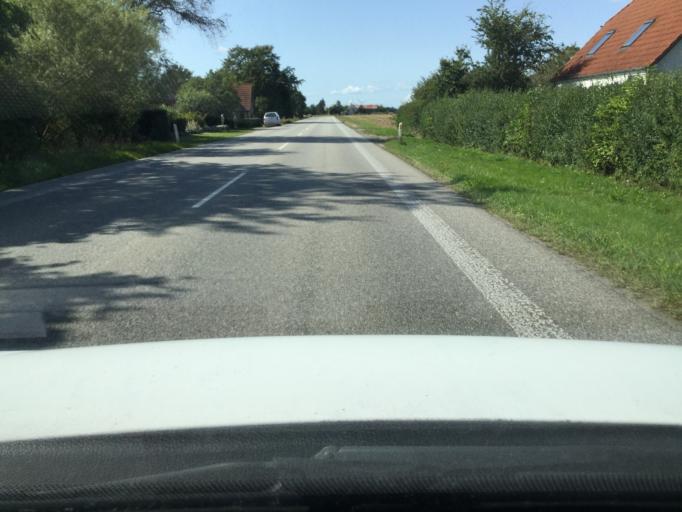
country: DK
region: Zealand
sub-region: Lolland Kommune
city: Rodby
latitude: 54.7630
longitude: 11.3210
